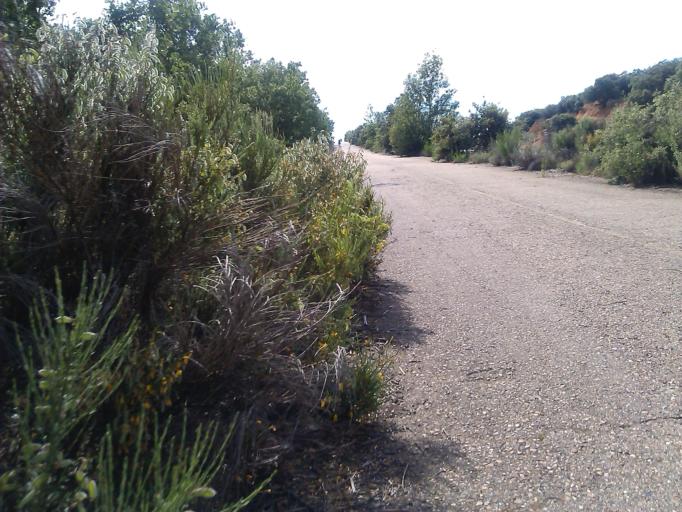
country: ES
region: Castille and Leon
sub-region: Provincia de Leon
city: San Justo de la Vega
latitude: 42.4480
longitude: -5.9773
